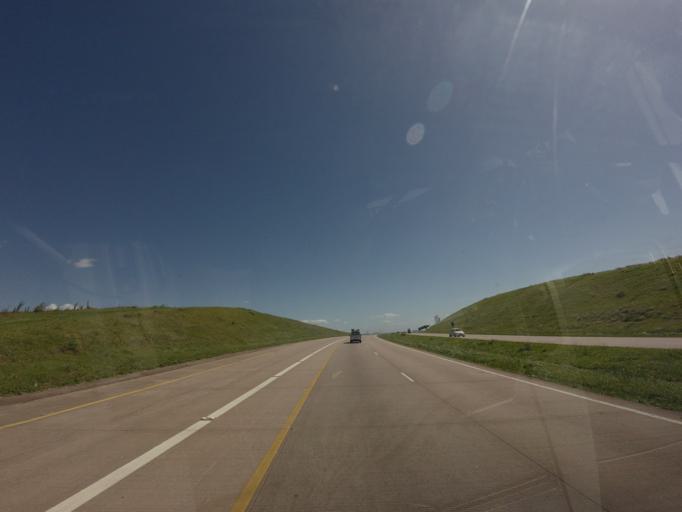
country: ZA
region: KwaZulu-Natal
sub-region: iLembe District Municipality
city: Stanger
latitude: -29.4228
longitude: 31.2736
